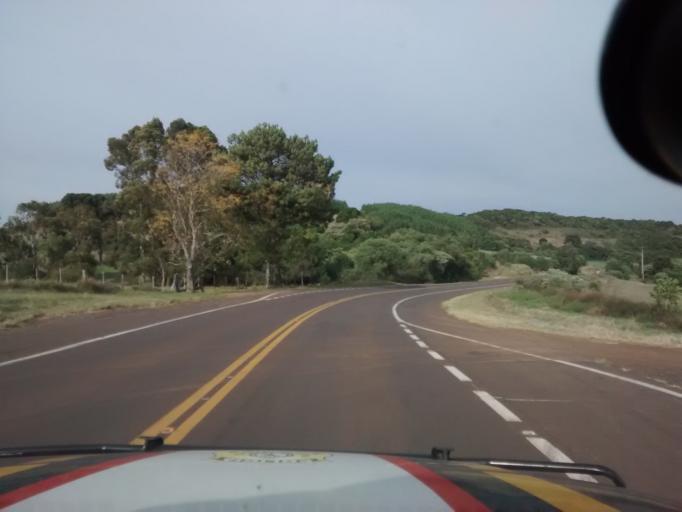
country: BR
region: Rio Grande do Sul
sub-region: Lagoa Vermelha
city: Lagoa Vermelha
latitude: -28.3317
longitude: -51.2903
